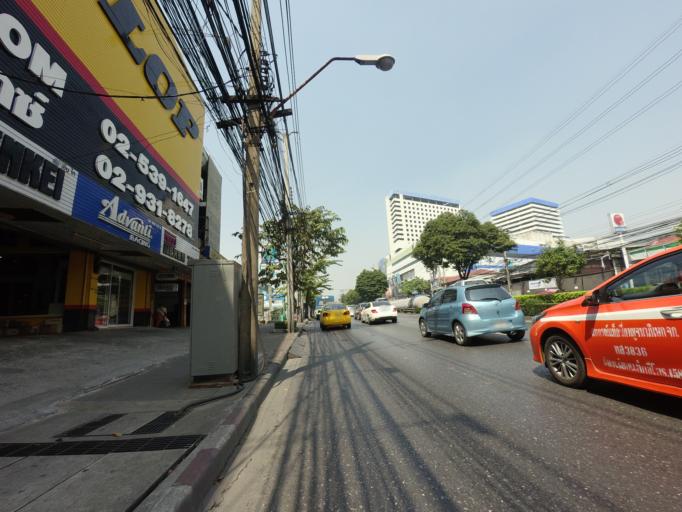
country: TH
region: Bangkok
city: Wang Thonglang
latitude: 13.7836
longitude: 100.6136
